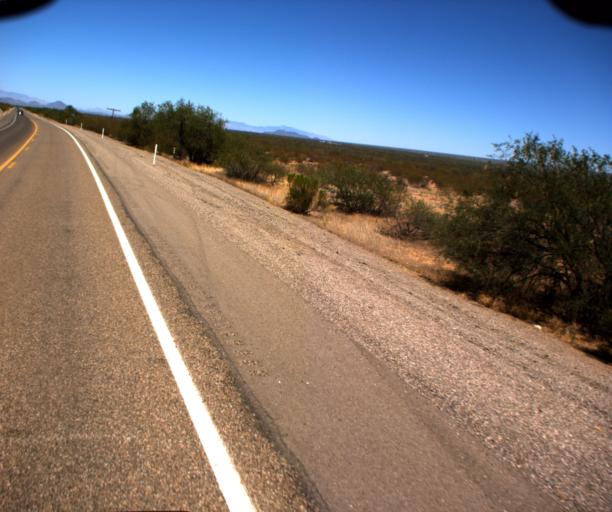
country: US
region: Arizona
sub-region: Pima County
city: Three Points
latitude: 32.0669
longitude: -111.3656
